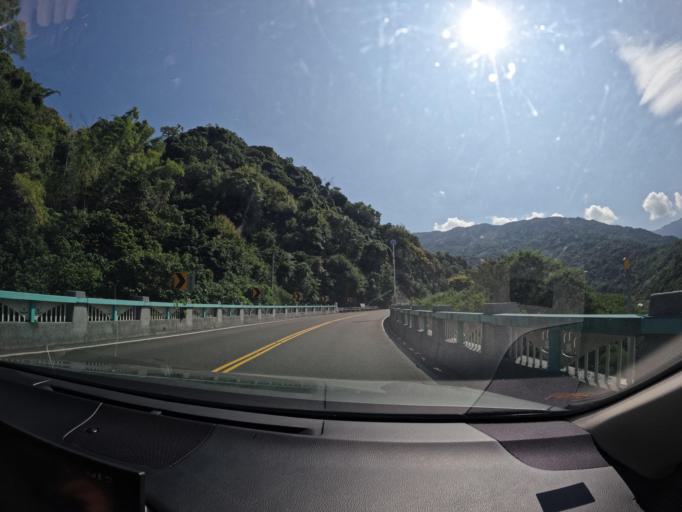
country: TW
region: Taiwan
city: Yujing
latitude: 23.1113
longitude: 120.7061
